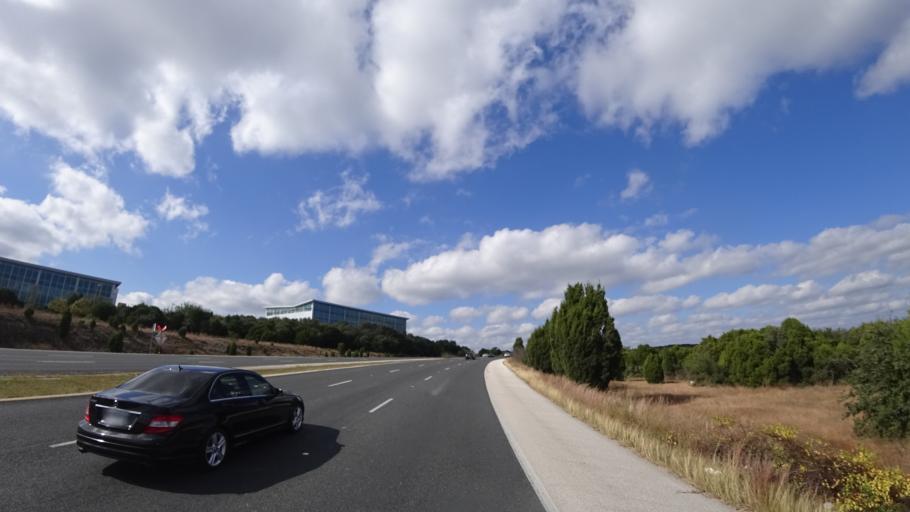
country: US
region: Texas
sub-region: Travis County
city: Barton Creek
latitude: 30.2524
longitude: -97.8617
